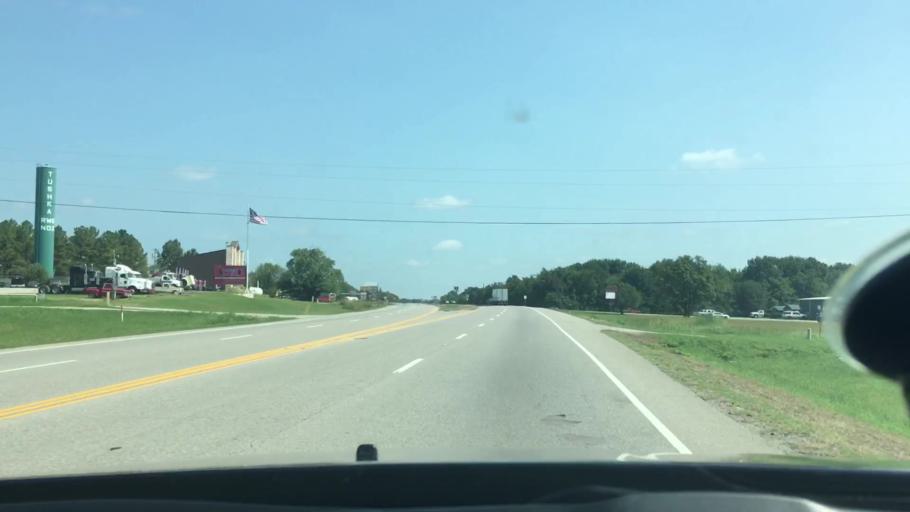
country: US
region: Oklahoma
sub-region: Atoka County
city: Atoka
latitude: 34.3438
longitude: -96.1522
